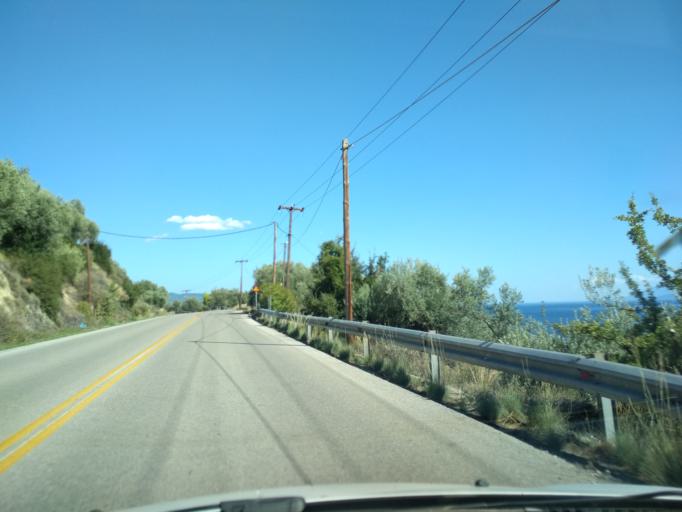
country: GR
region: Central Greece
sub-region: Nomos Evvoias
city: Oreoi
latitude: 38.8451
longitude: 23.1144
